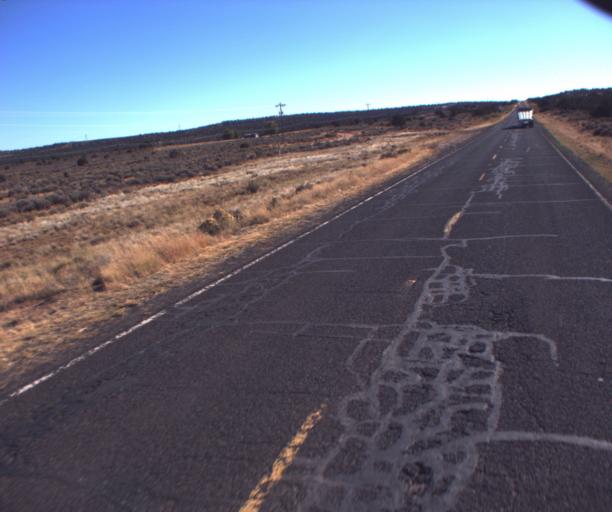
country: US
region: Arizona
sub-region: Apache County
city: Ganado
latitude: 35.6949
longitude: -109.5456
